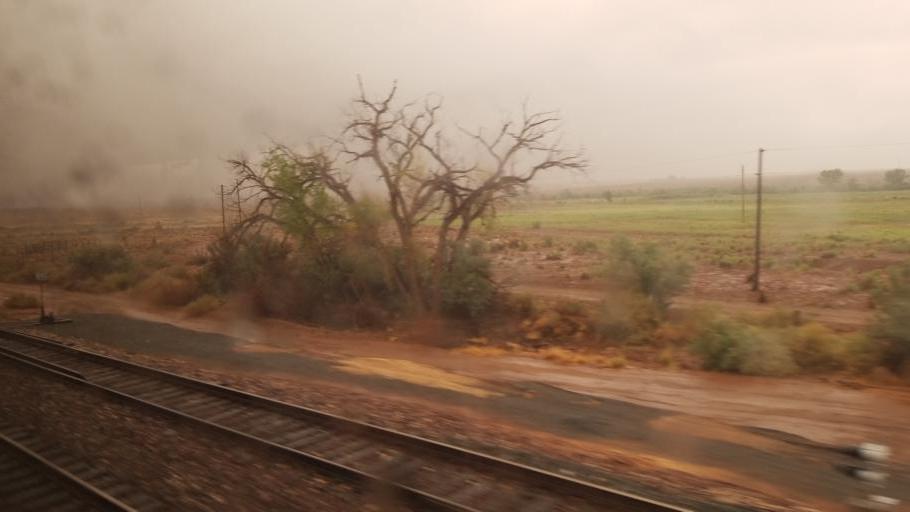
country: US
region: Arizona
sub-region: Navajo County
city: Joseph City
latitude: 34.9095
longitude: -110.2616
